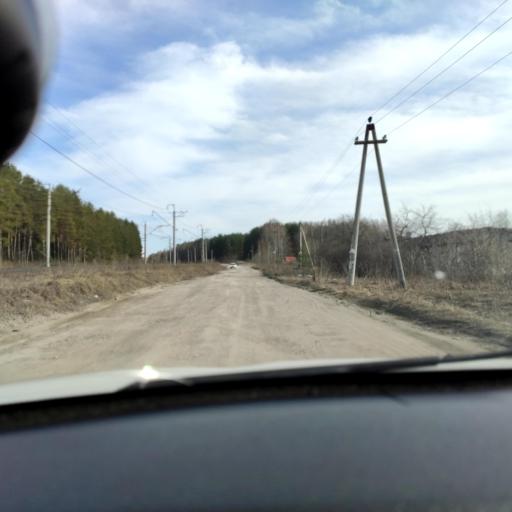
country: RU
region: Perm
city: Overyata
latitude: 58.0574
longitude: 55.9918
